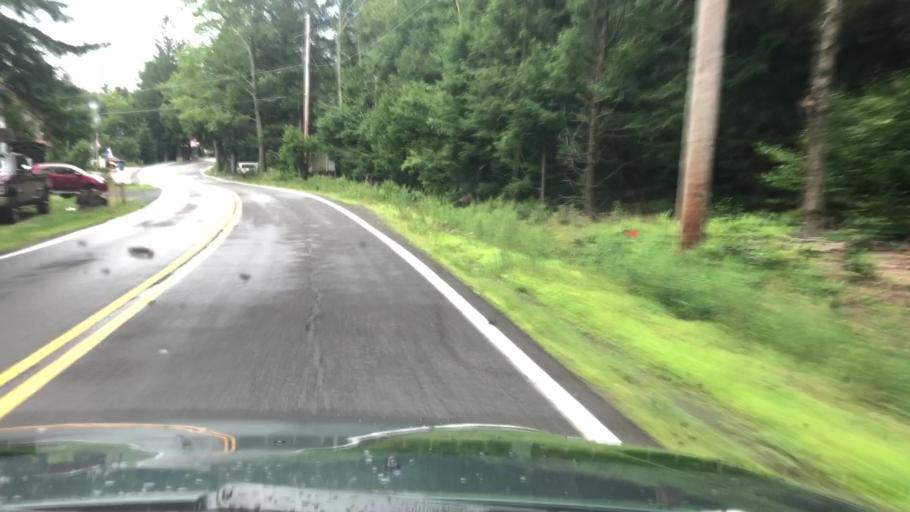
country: US
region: Pennsylvania
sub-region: Monroe County
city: Mountainhome
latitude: 41.3089
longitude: -75.2108
